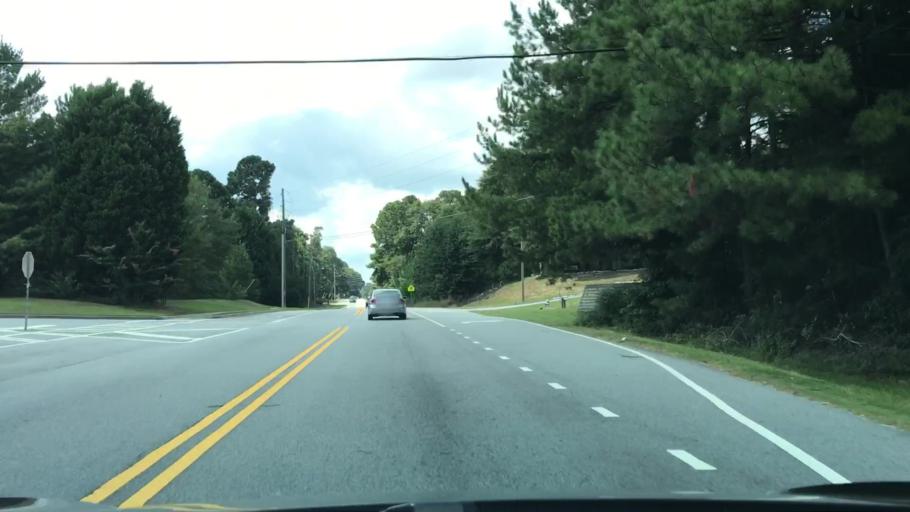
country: US
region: Georgia
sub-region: Gwinnett County
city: Lawrenceville
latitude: 33.9502
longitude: -84.0607
